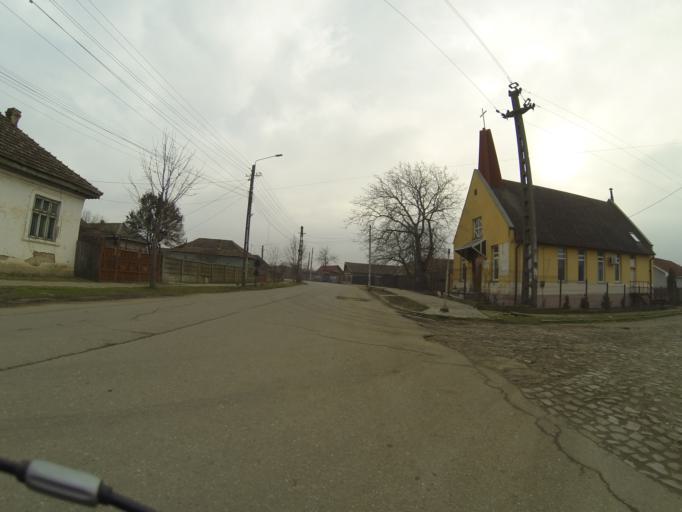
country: RO
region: Mehedinti
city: Vanju-Mare
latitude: 44.4224
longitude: 22.8724
